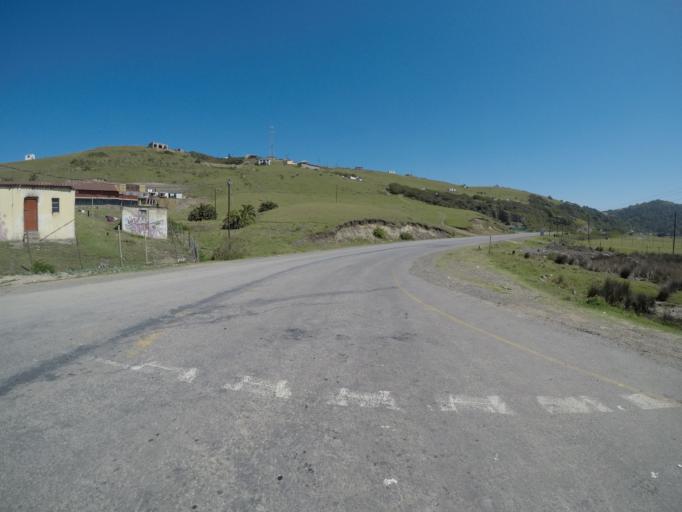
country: ZA
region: Eastern Cape
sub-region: OR Tambo District Municipality
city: Libode
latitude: -31.9836
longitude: 29.1478
